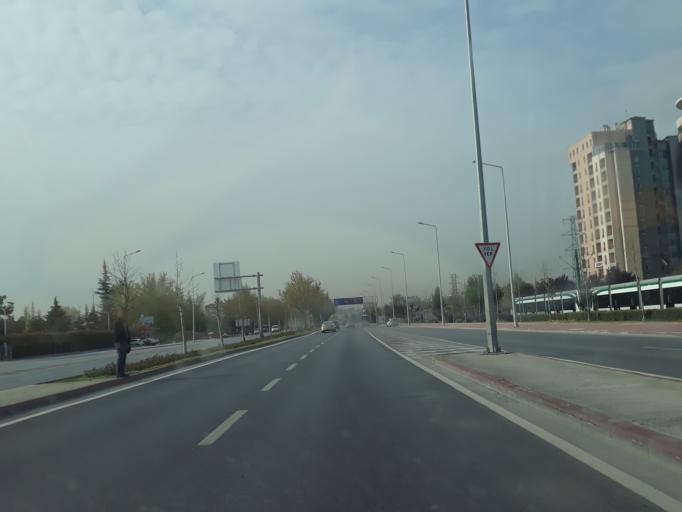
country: TR
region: Konya
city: Selcuklu
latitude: 37.9554
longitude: 32.5136
